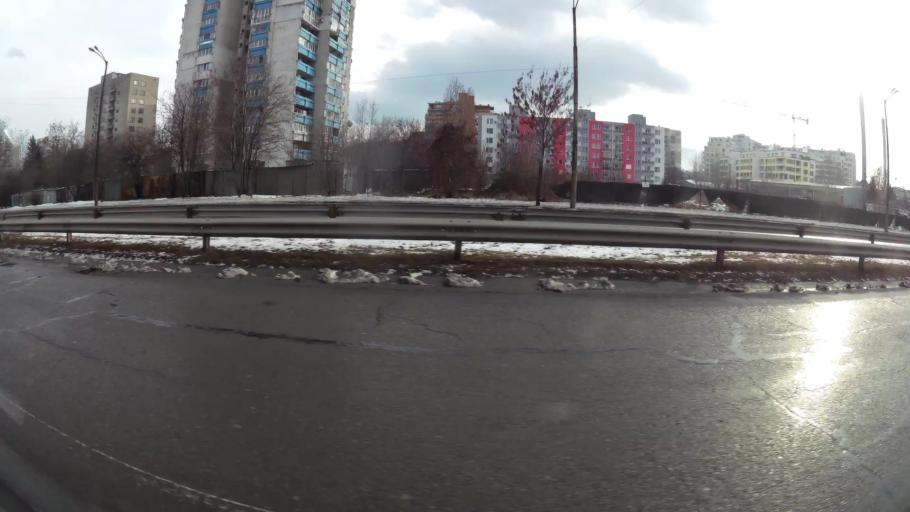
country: BG
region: Sofia-Capital
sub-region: Stolichna Obshtina
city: Sofia
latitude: 42.7118
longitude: 23.3582
